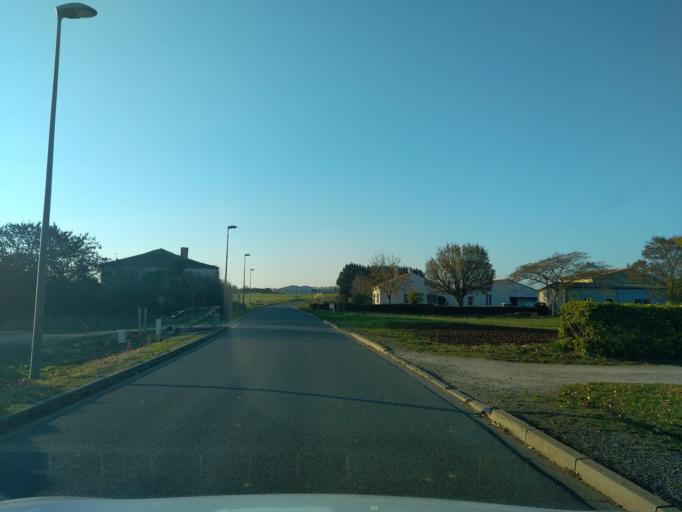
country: FR
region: Pays de la Loire
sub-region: Departement de la Vendee
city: Maillezais
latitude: 46.3373
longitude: -0.7642
